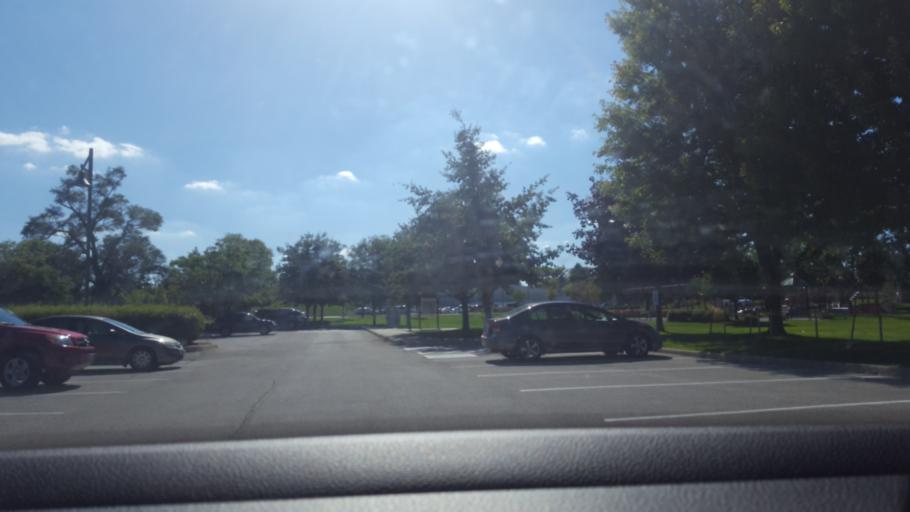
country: CA
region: Ontario
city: Burlington
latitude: 43.3364
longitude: -79.7911
